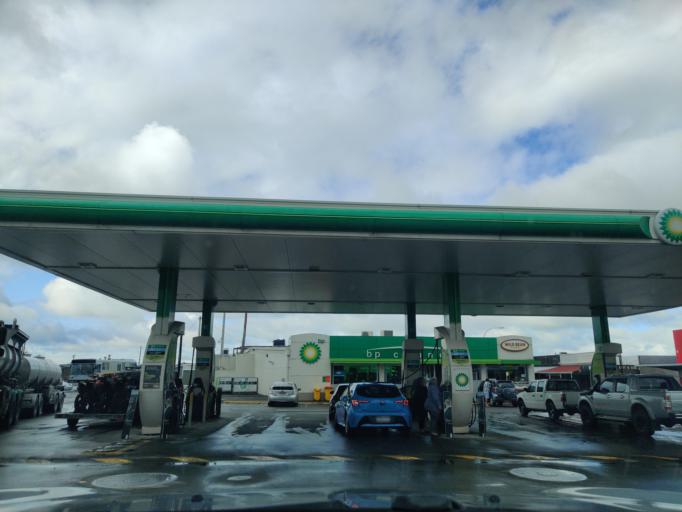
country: NZ
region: Manawatu-Wanganui
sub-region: Palmerston North City
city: Palmerston North
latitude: -40.2099
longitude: 176.0947
